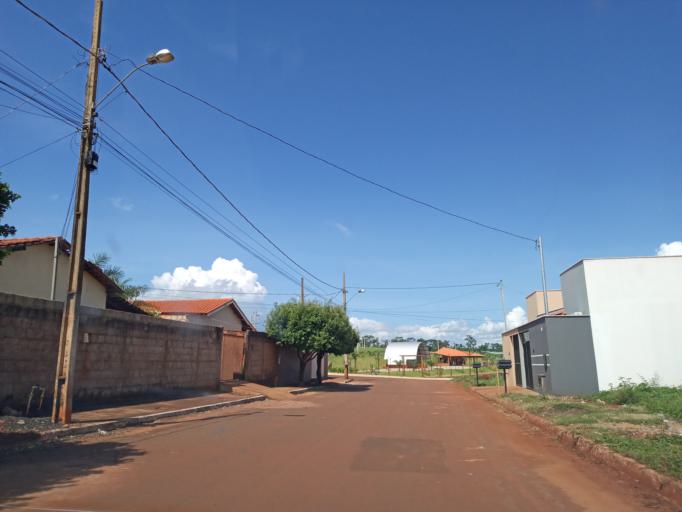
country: BR
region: Goias
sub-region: Itumbiara
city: Itumbiara
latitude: -18.4335
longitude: -49.1828
